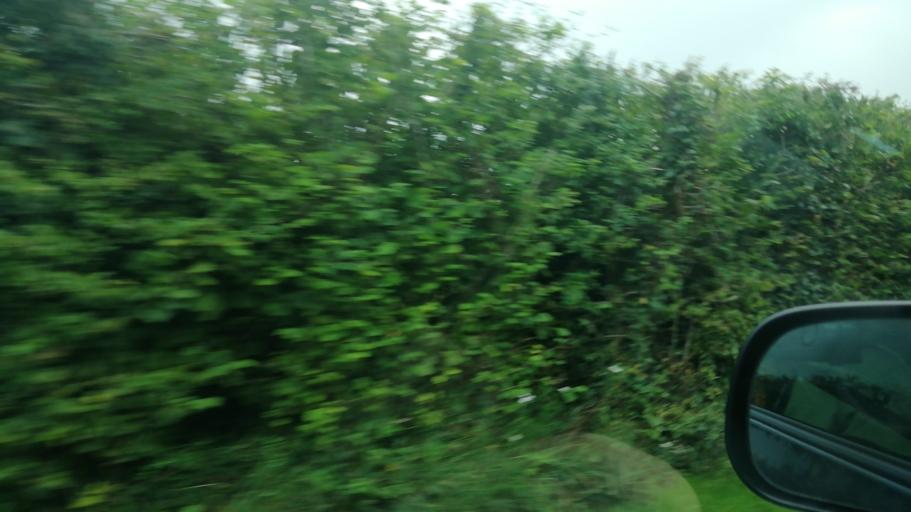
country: IE
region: Munster
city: Fethard
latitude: 52.5122
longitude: -7.6850
